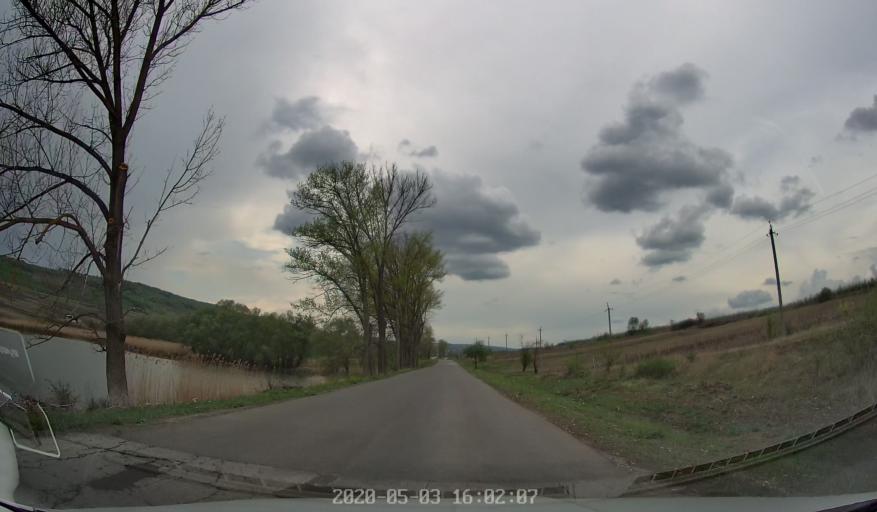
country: MD
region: Stinga Nistrului
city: Bucovat
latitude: 47.1709
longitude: 28.4000
